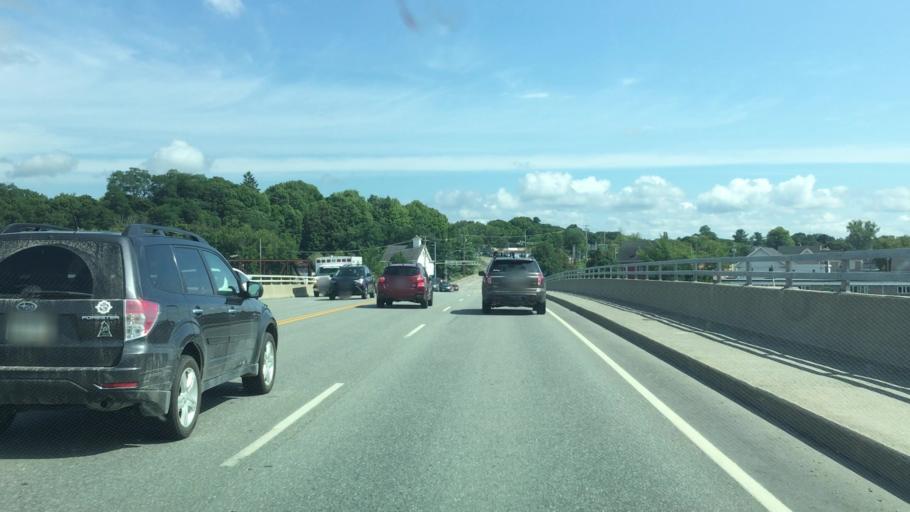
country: US
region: Maine
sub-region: Penobscot County
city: Brewer
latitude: 44.7992
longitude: -68.7646
